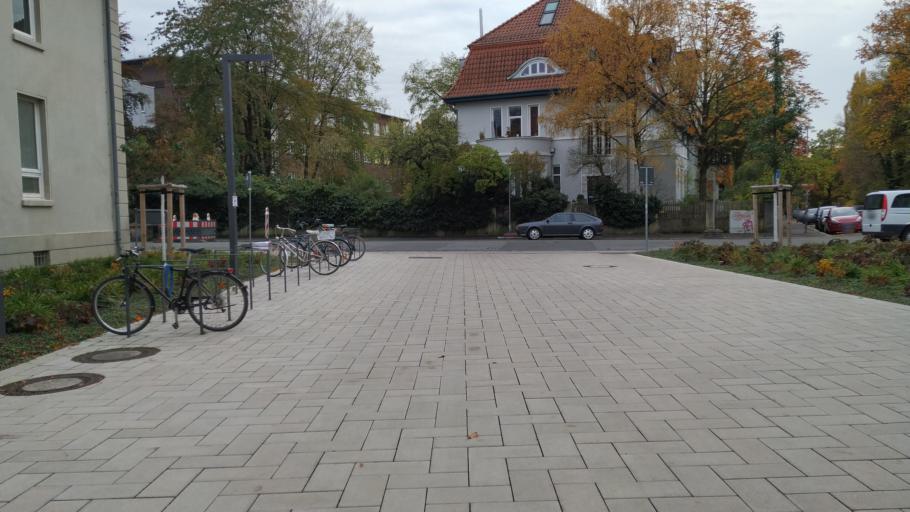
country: DE
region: Lower Saxony
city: Hannover
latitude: 52.3877
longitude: 9.7127
